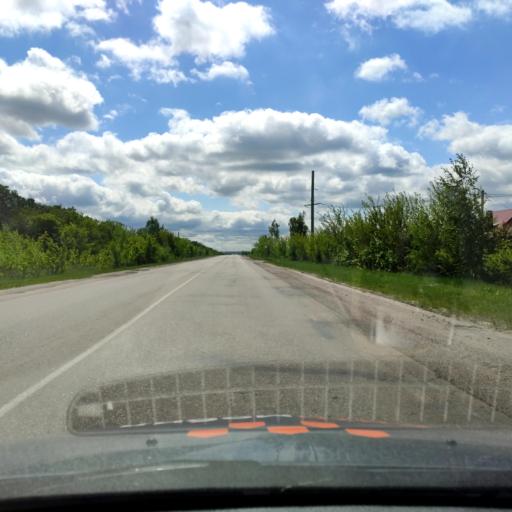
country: RU
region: Voronezj
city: Novaya Usman'
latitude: 51.6183
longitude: 39.3358
